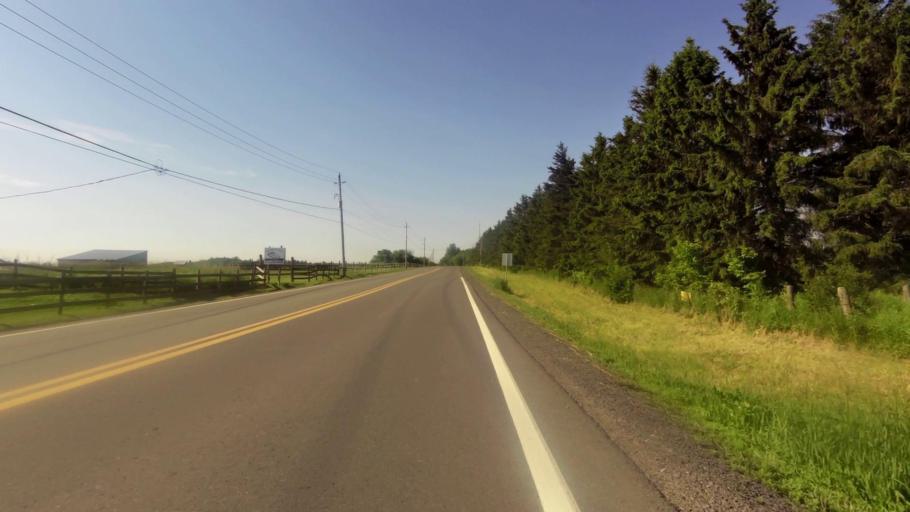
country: CA
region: Ontario
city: Ottawa
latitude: 45.2393
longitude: -75.5610
